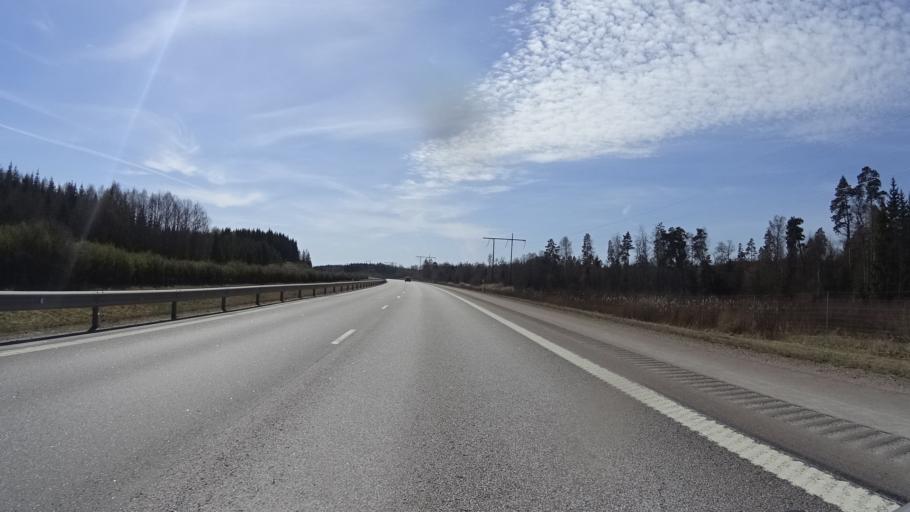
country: SE
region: OEstergoetland
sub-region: Vadstena Kommun
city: Herrestad
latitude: 58.2839
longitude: 14.8731
